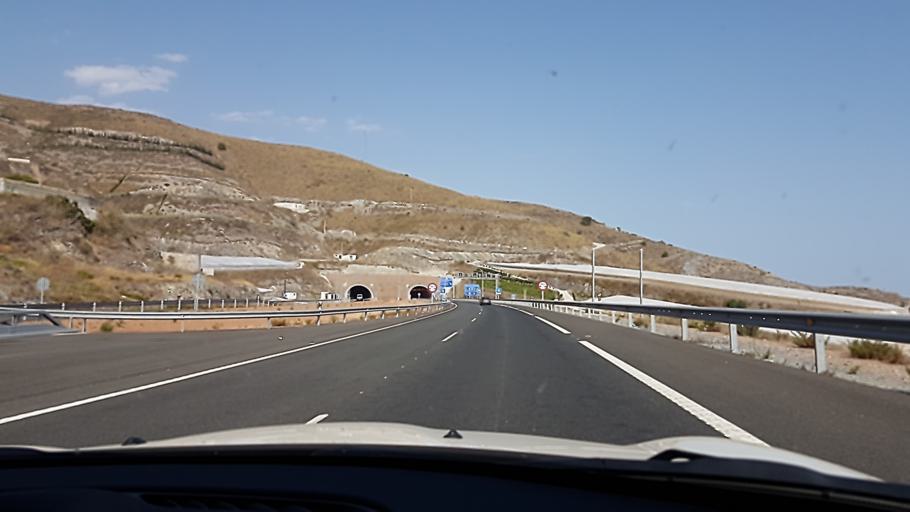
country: ES
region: Andalusia
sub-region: Provincia de Granada
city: Gualchos
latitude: 36.7157
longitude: -3.4484
